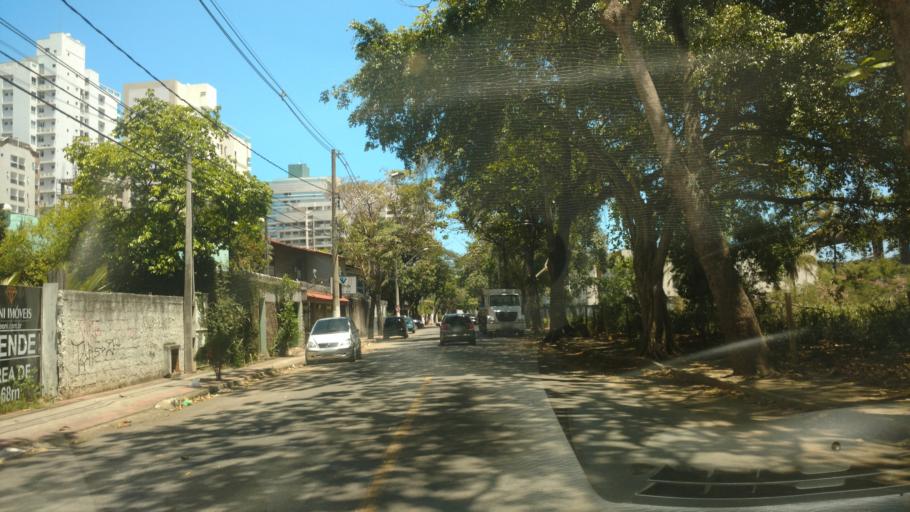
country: BR
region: Espirito Santo
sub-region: Vila Velha
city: Vila Velha
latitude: -20.3297
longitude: -40.2814
